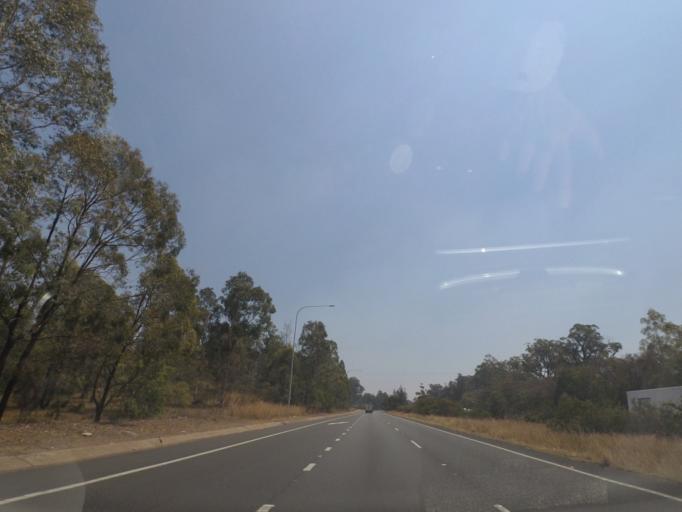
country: AU
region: New South Wales
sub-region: Newcastle
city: Beresfield
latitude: -32.8323
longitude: 151.6344
